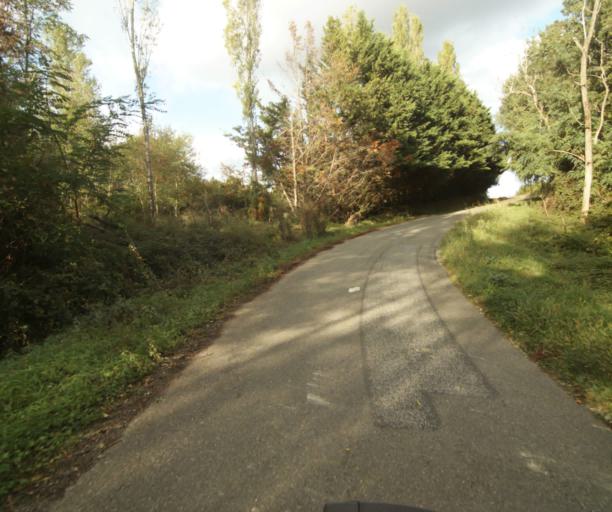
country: FR
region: Midi-Pyrenees
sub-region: Departement de la Haute-Garonne
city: Launac
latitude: 43.8356
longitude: 1.1191
